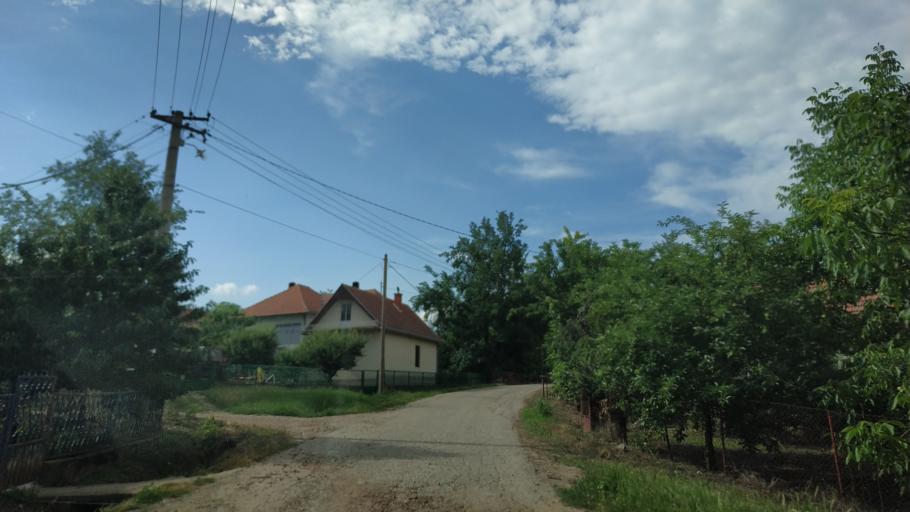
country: RS
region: Central Serbia
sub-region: Nisavski Okrug
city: Aleksinac
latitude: 43.6161
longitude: 21.6463
